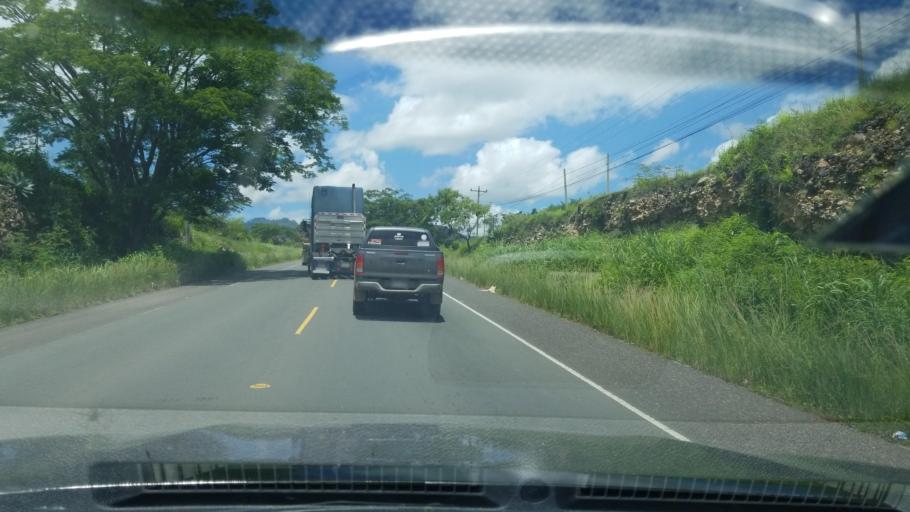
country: HN
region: Francisco Morazan
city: Cofradia
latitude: 14.2635
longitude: -87.2450
